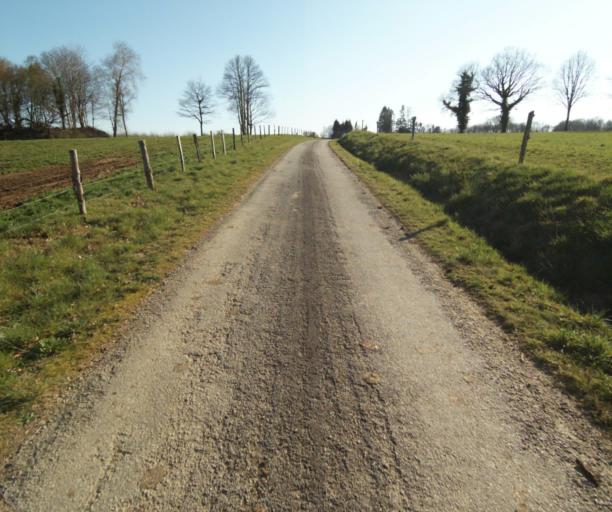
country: FR
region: Limousin
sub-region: Departement de la Correze
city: Chamboulive
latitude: 45.4785
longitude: 1.7274
